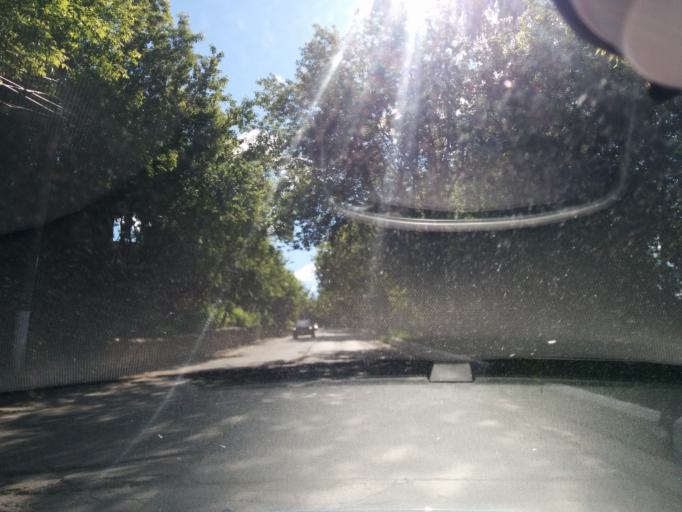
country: RU
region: Perm
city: Perm
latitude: 58.0138
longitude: 56.2065
